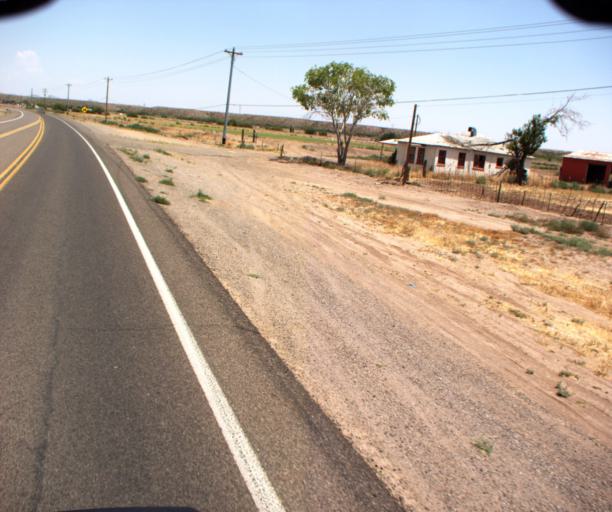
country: US
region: Arizona
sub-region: Graham County
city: Safford
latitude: 32.8131
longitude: -109.6185
